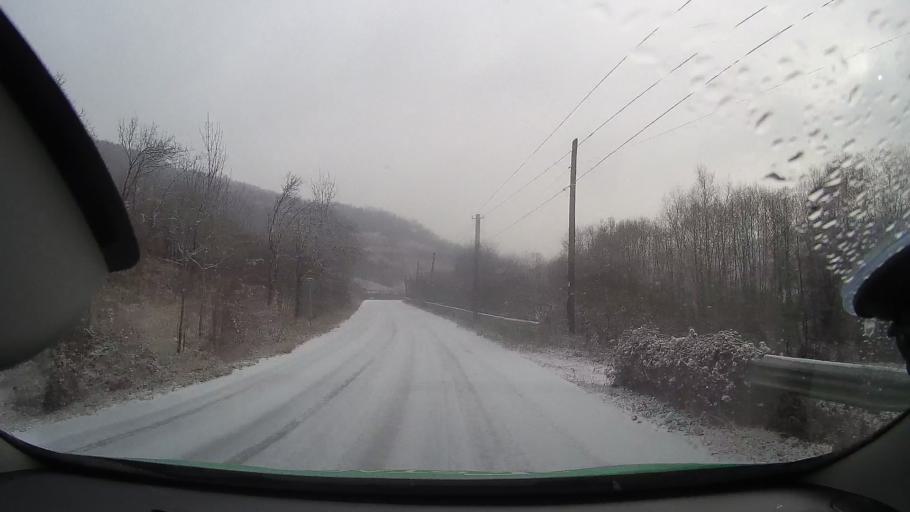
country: RO
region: Alba
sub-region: Comuna Livezile
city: Livezile
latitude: 46.3687
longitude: 23.5897
